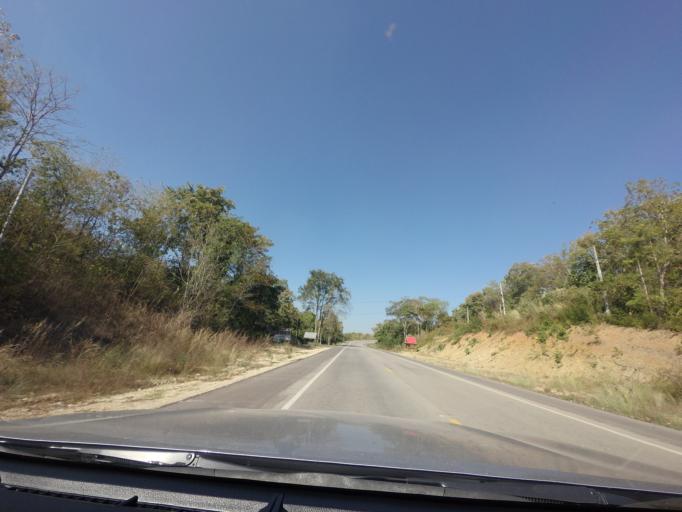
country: TH
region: Lampang
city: Mae Mo
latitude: 18.4813
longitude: 99.6355
